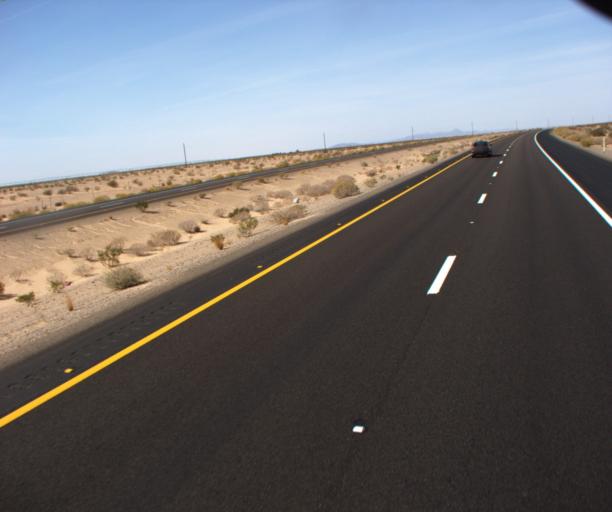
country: US
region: Arizona
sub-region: Yuma County
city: Somerton
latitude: 32.5108
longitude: -114.5594
